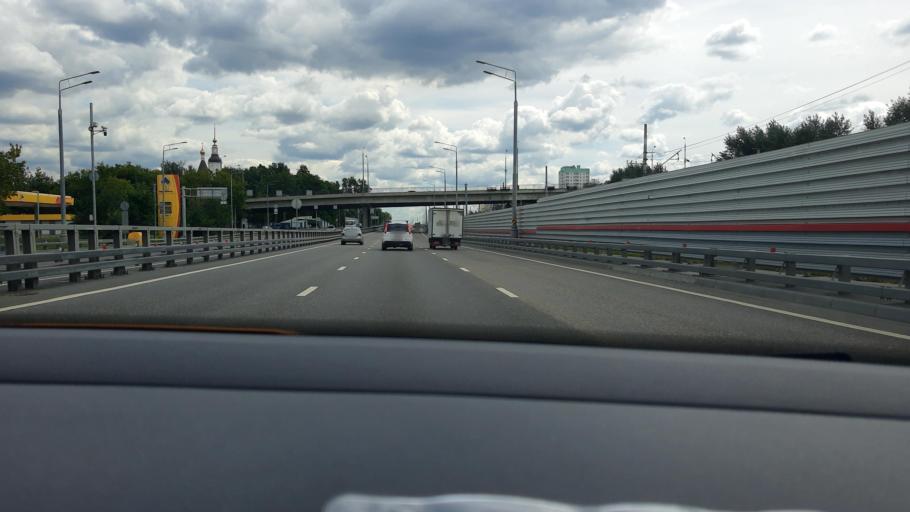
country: RU
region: Moscow
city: Perovo
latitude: 55.7253
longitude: 37.7940
